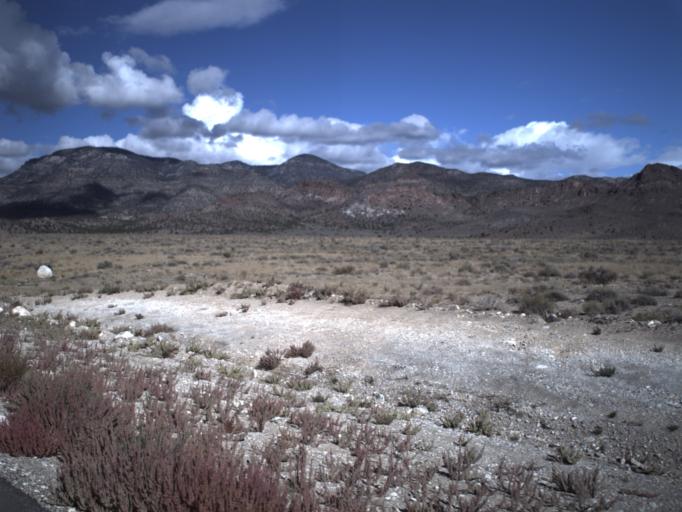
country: US
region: Utah
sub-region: Beaver County
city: Milford
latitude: 38.4943
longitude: -113.4802
